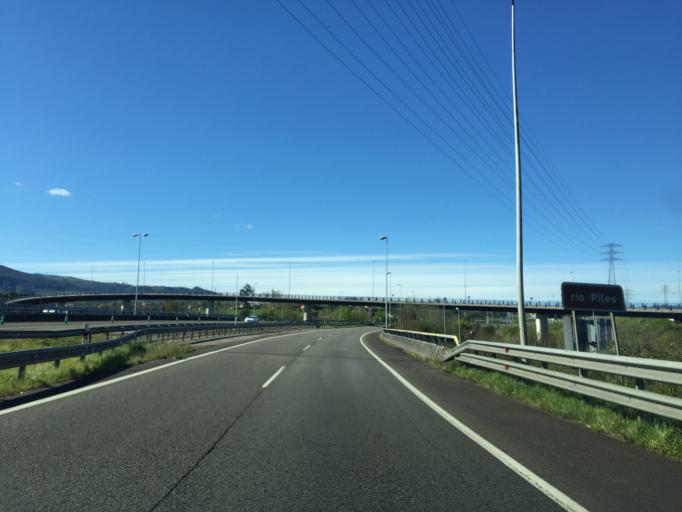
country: ES
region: Asturias
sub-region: Province of Asturias
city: Gijon
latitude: 43.5174
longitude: -5.6554
